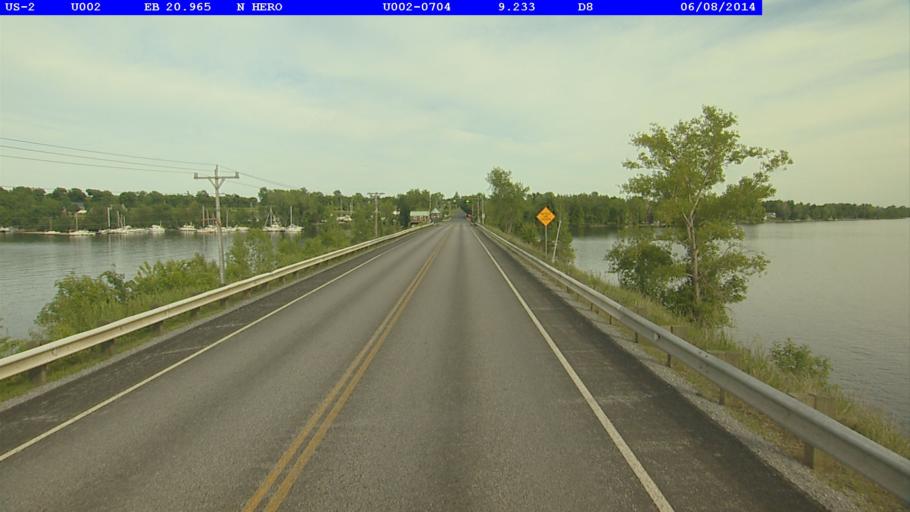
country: US
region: Vermont
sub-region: Grand Isle County
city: North Hero
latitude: 44.7673
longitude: -73.2914
